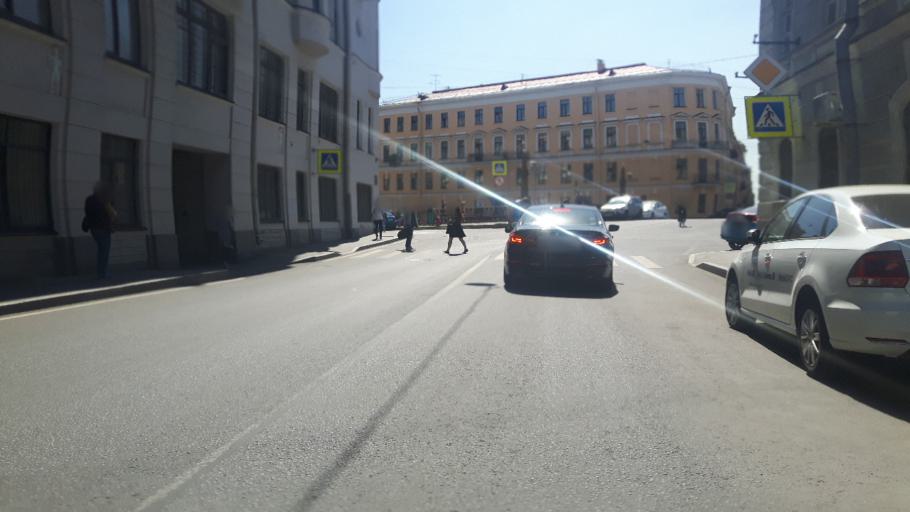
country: RU
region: St.-Petersburg
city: Saint Petersburg
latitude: 59.9274
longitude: 30.3057
